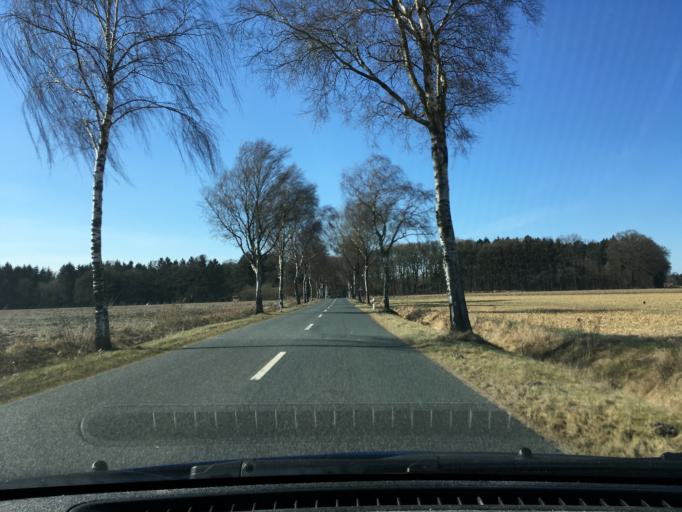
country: DE
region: Lower Saxony
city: Schneverdingen
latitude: 53.0809
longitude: 9.8293
